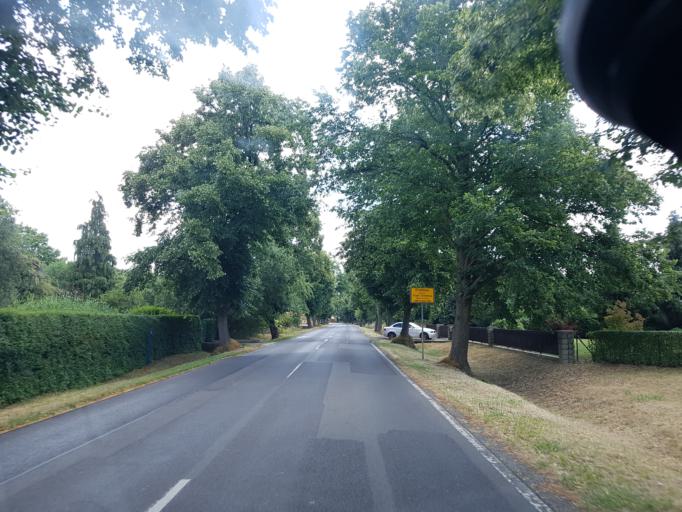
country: DE
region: Brandenburg
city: Drebkau
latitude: 51.6599
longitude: 14.2113
